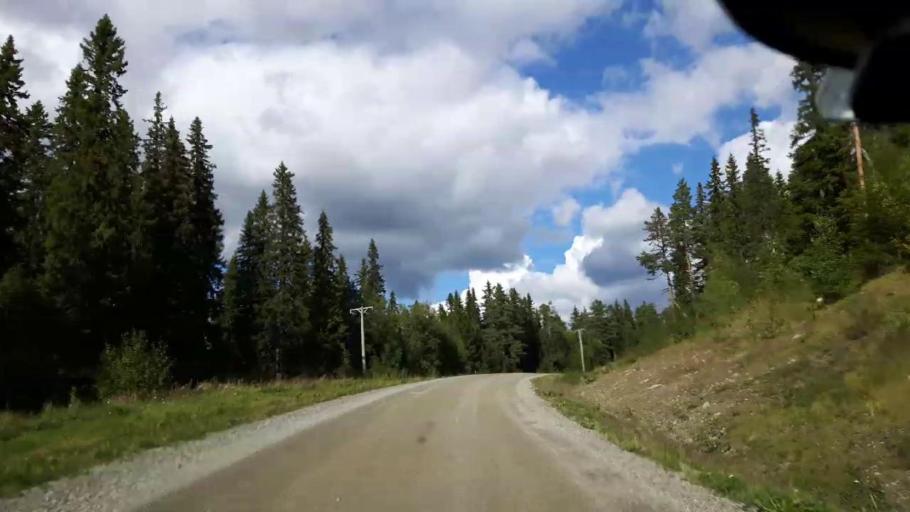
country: SE
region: Jaemtland
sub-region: Stroemsunds Kommun
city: Stroemsund
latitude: 63.3420
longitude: 15.5662
